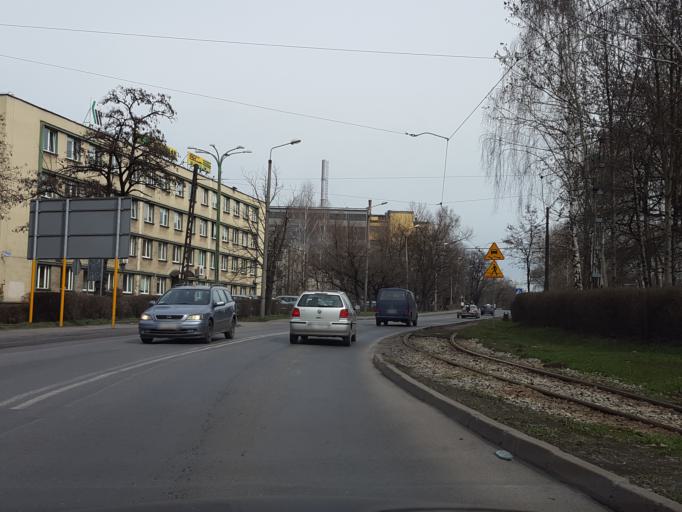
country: PL
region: Silesian Voivodeship
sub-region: Ruda Slaska
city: Ruda Slaska
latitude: 50.2762
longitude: 18.8704
